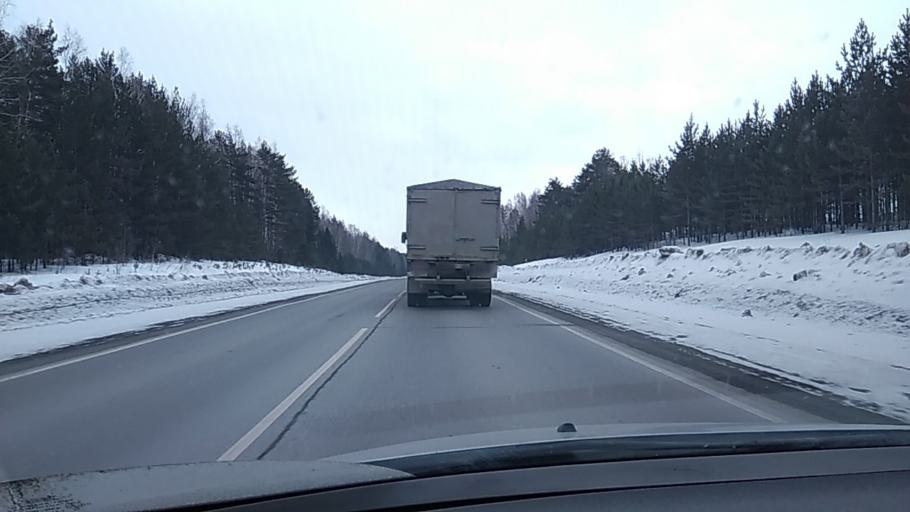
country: RU
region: Sverdlovsk
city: Verkhneye Dubrovo
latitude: 56.7142
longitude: 61.0596
